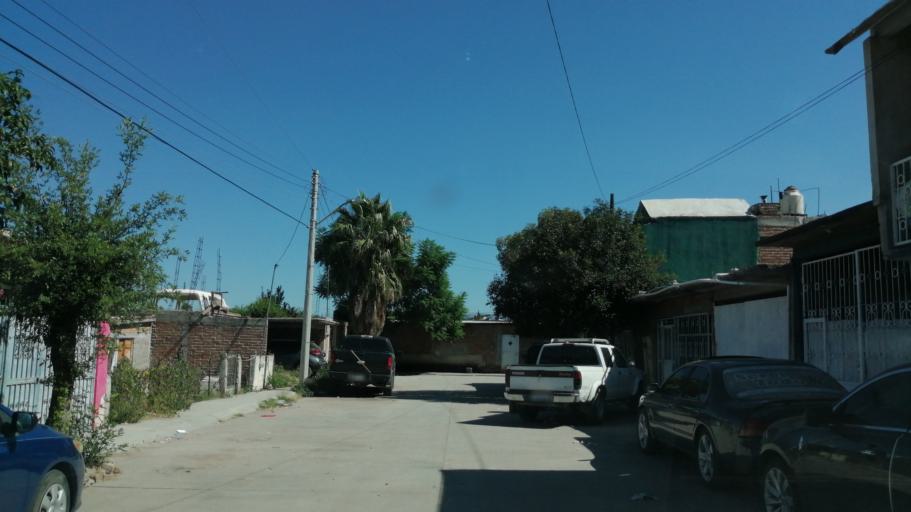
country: MX
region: Durango
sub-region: Santiago Papasquiaro
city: Santiago Papasquiaro
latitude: 25.0507
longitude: -105.4359
